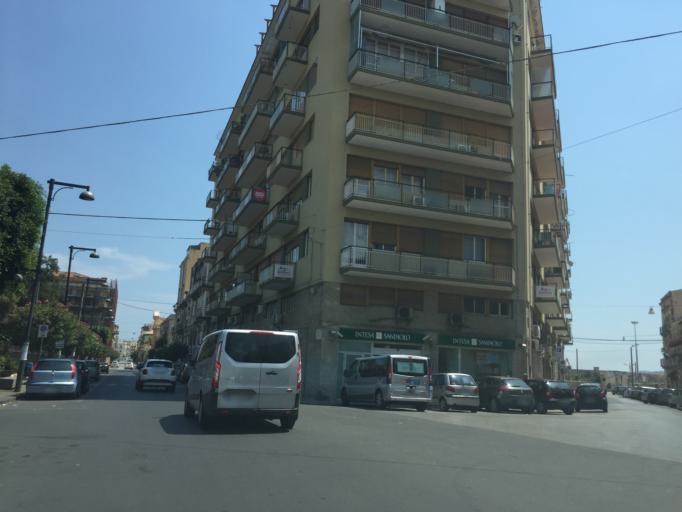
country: IT
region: Sicily
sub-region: Provincia di Siracusa
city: Siracusa
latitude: 37.0661
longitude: 15.2840
